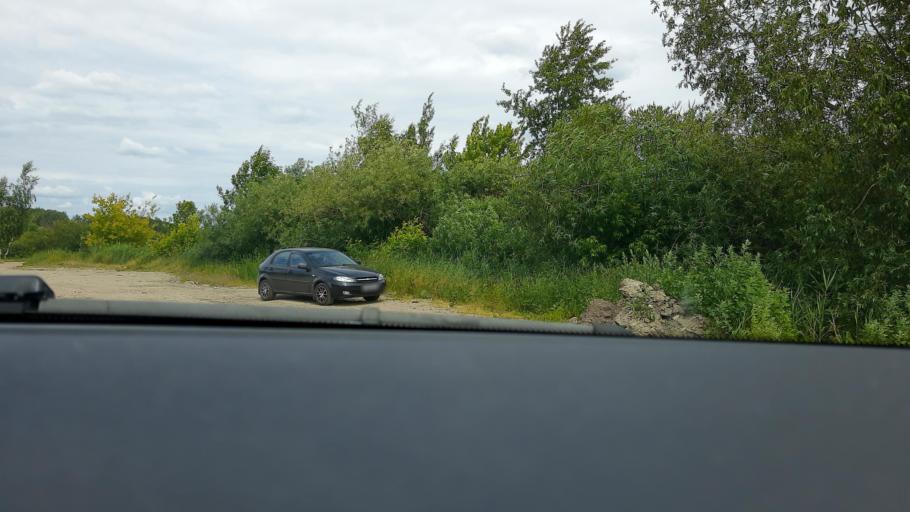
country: RU
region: Nizjnij Novgorod
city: Gorbatovka
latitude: 56.2605
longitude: 43.8106
